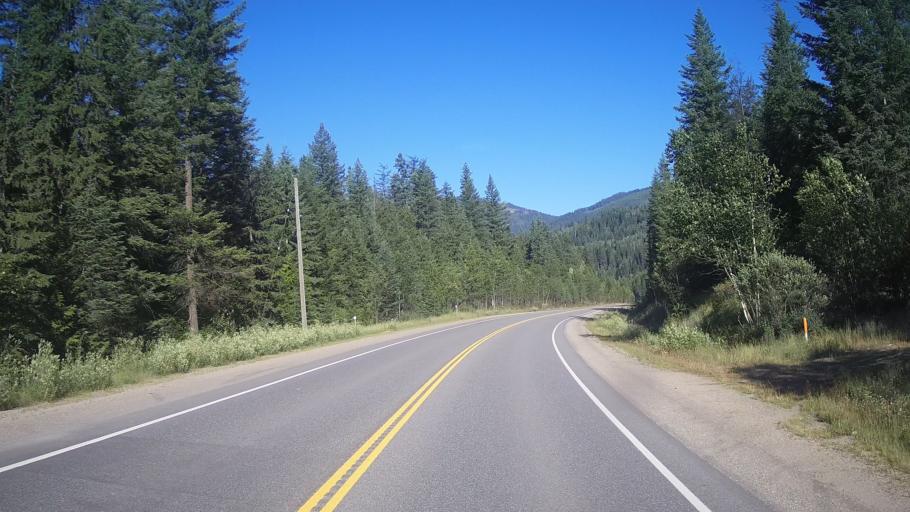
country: CA
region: British Columbia
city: Chase
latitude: 51.6699
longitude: -119.5963
